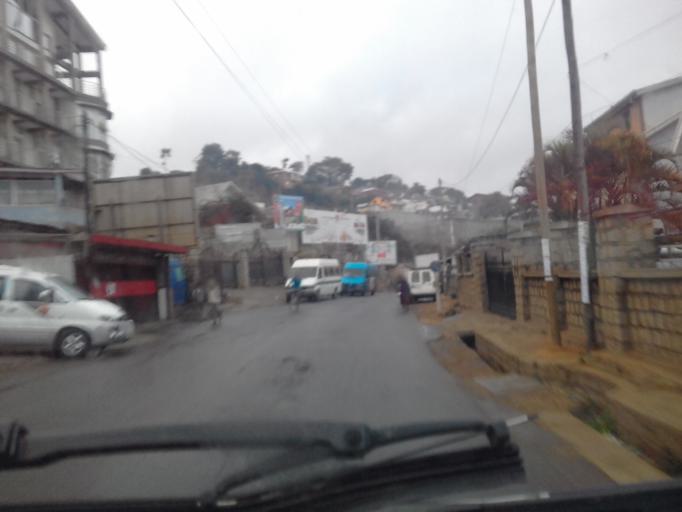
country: MG
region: Analamanga
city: Antananarivo
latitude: -18.8696
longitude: 47.5517
